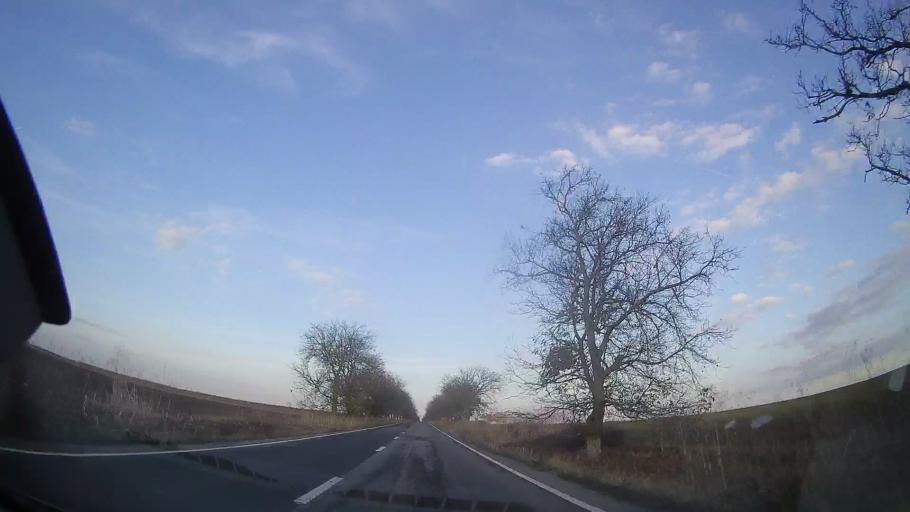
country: RO
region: Constanta
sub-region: Comuna Chirnogeni
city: Chirnogeni
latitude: 43.8604
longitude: 28.2576
